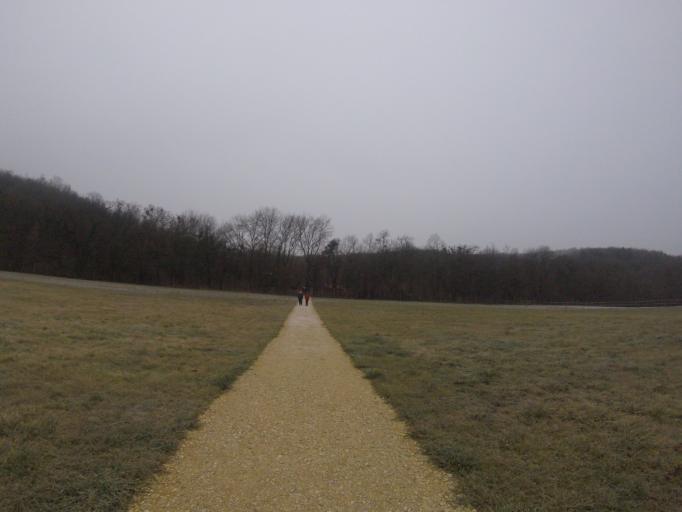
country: HU
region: Fejer
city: Bicske
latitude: 47.4212
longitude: 18.5836
